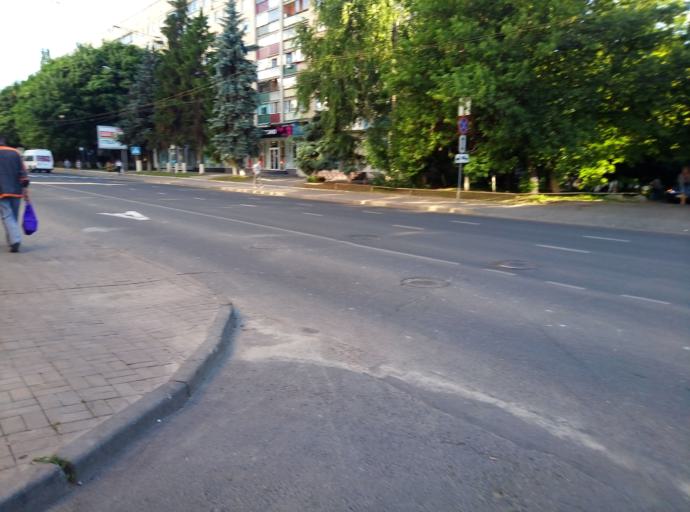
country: RU
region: Kursk
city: Kursk
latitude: 51.7495
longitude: 36.1903
